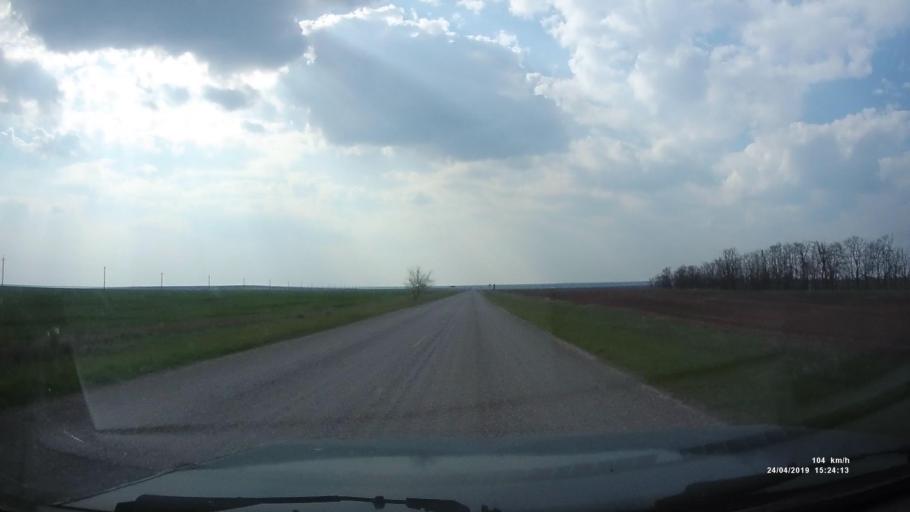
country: RU
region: Rostov
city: Remontnoye
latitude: 46.5469
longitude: 43.0730
